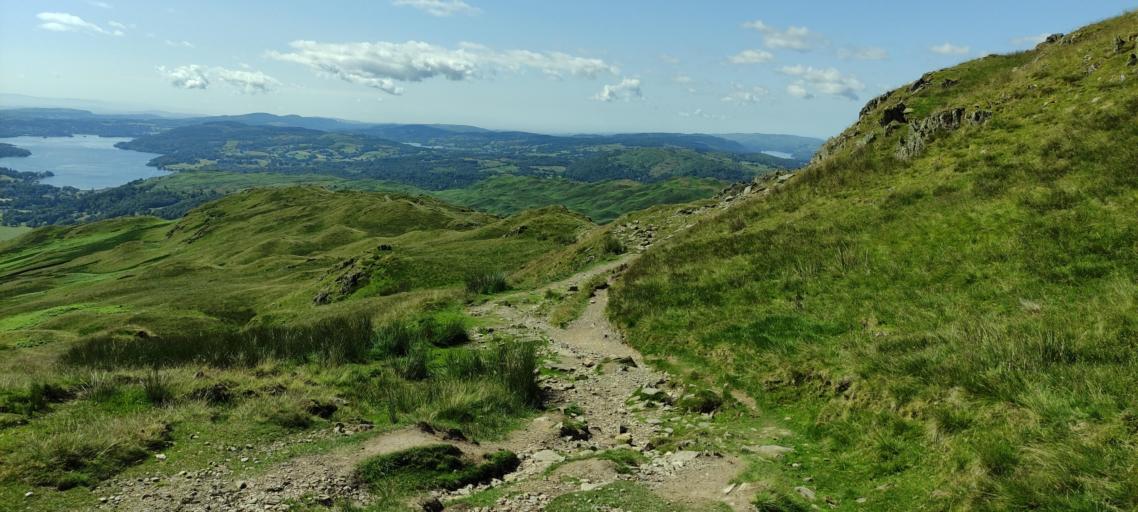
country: GB
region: England
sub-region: Cumbria
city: Ambleside
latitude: 54.4612
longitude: -2.9963
